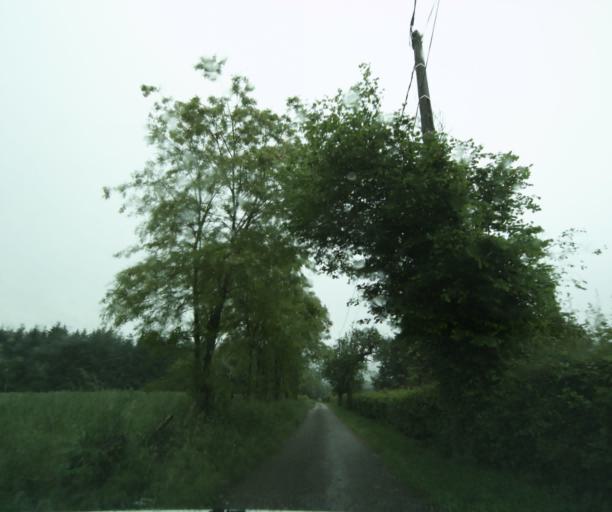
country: FR
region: Bourgogne
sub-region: Departement de Saone-et-Loire
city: Charolles
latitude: 46.3884
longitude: 4.3738
